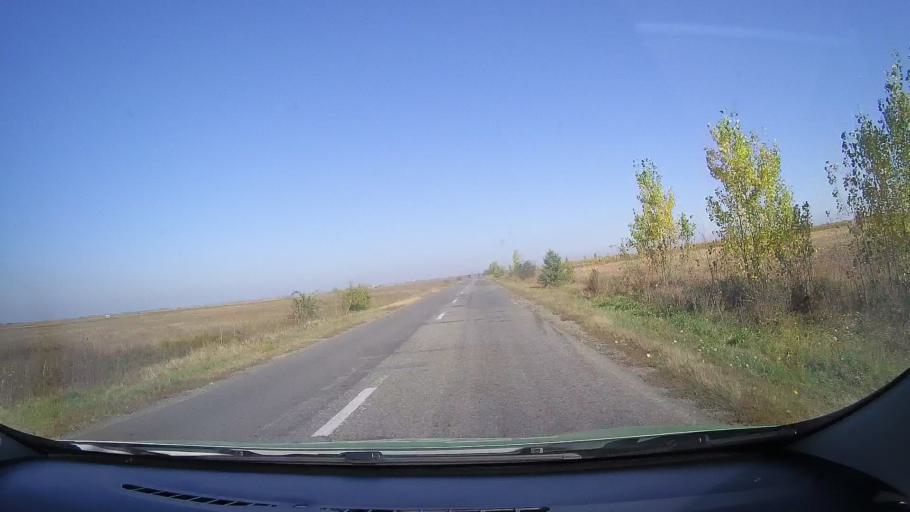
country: RO
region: Satu Mare
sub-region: Comuna Cauas
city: Cauas
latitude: 47.5285
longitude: 22.5675
